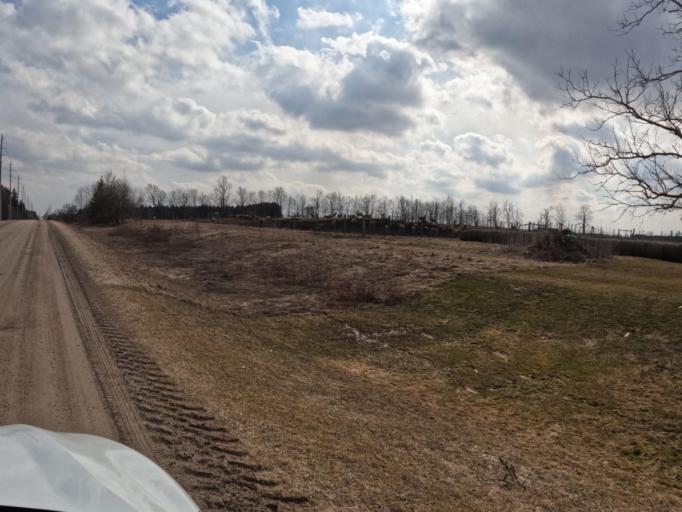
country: CA
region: Ontario
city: Shelburne
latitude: 43.9756
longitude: -80.3025
